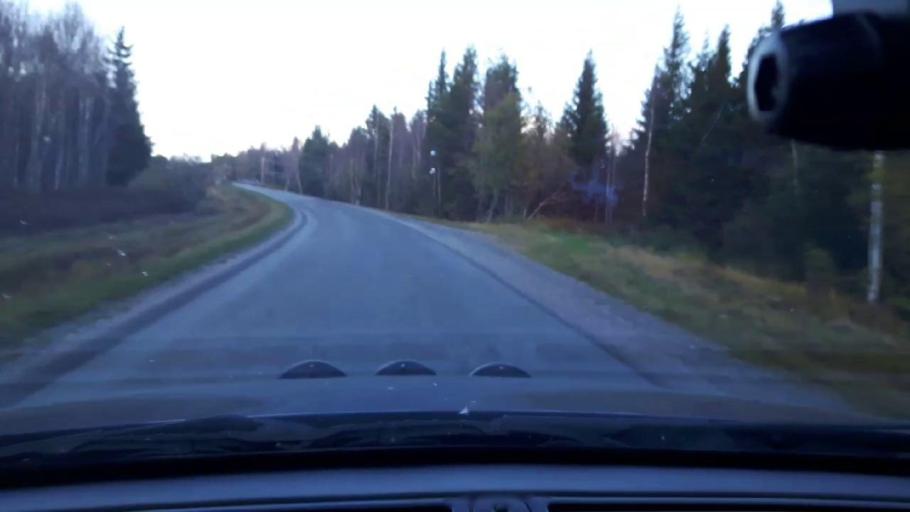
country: SE
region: Jaemtland
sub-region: Bergs Kommun
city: Hoverberg
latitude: 63.0674
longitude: 14.2658
